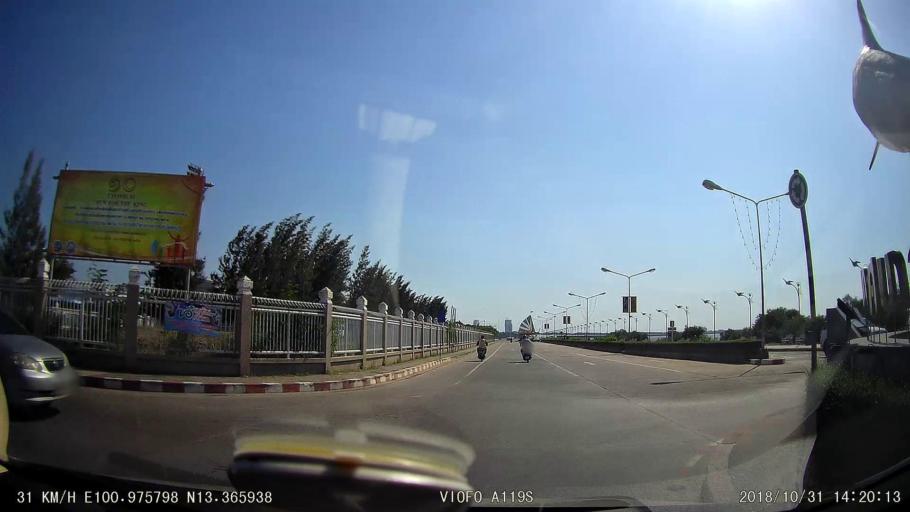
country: TH
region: Chon Buri
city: Chon Buri
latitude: 13.3658
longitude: 100.9758
